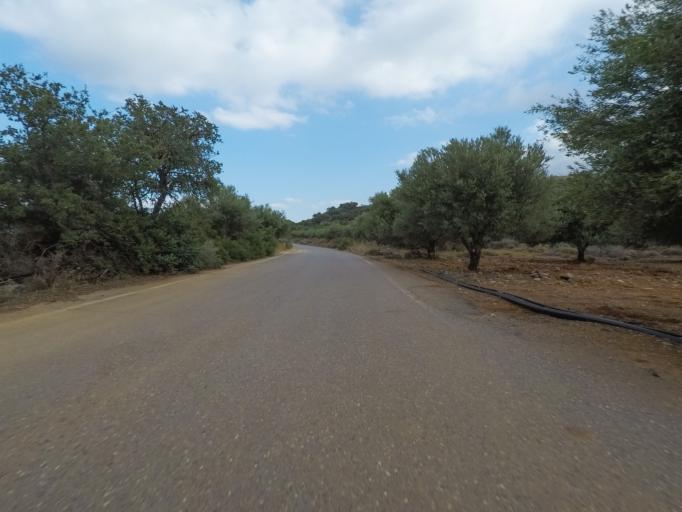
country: GR
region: Crete
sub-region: Nomos Lasithiou
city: Kritsa
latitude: 35.1709
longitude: 25.6536
